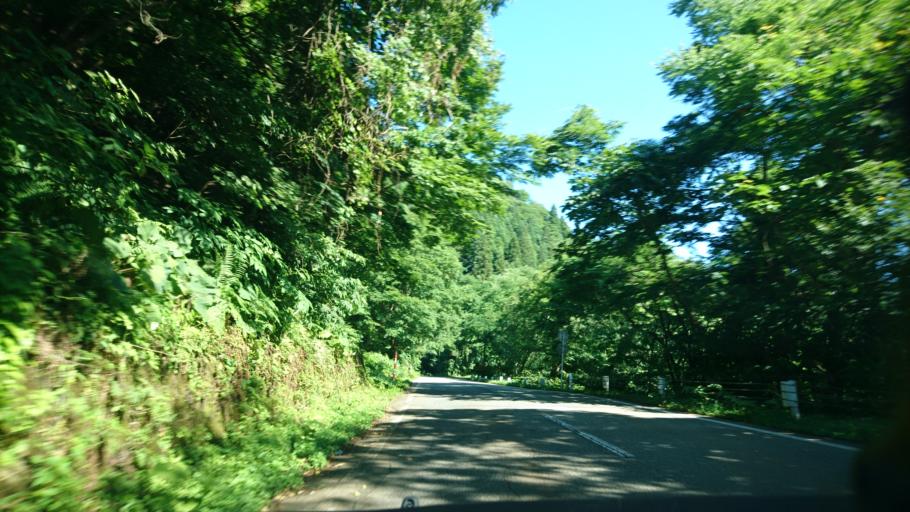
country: JP
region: Akita
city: Kakunodatemachi
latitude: 39.7305
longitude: 140.6320
